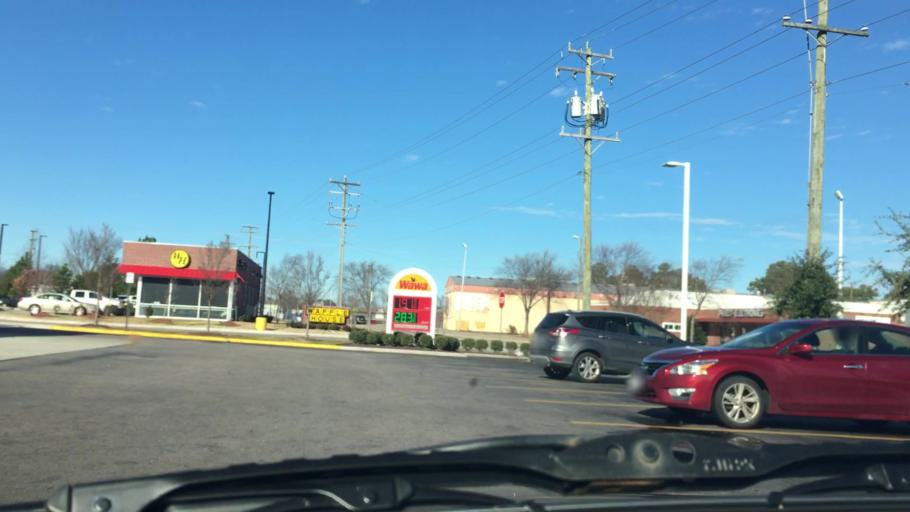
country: US
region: Virginia
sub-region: City of Norfolk
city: Norfolk
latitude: 36.8633
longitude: -76.2448
